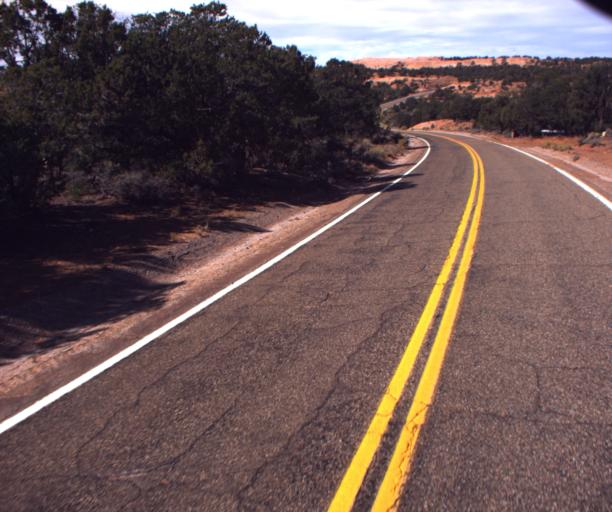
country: US
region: Arizona
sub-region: Navajo County
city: Kayenta
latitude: 36.6559
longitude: -110.5213
